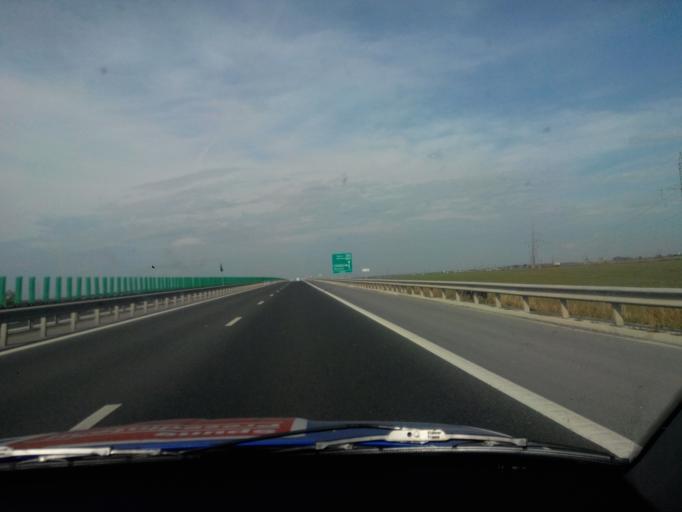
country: RO
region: Constanta
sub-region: Comuna Cumpana
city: Cumpana
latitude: 44.1306
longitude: 28.5741
